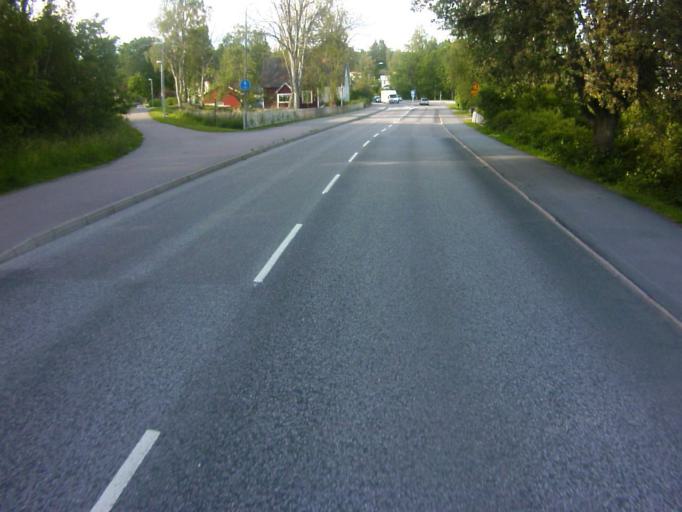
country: SE
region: Soedermanland
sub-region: Eskilstuna Kommun
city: Skogstorp
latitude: 59.3243
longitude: 16.4811
